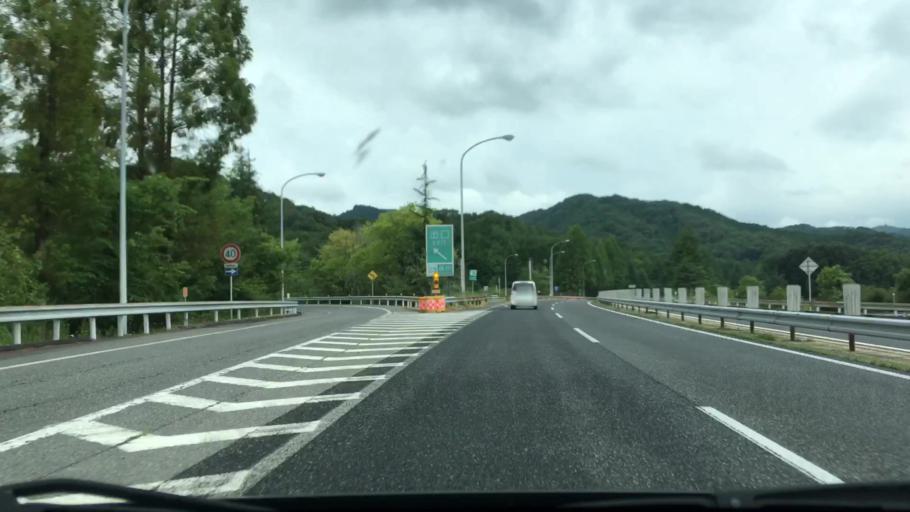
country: JP
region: Hiroshima
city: Miyoshi
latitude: 34.7193
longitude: 132.6836
